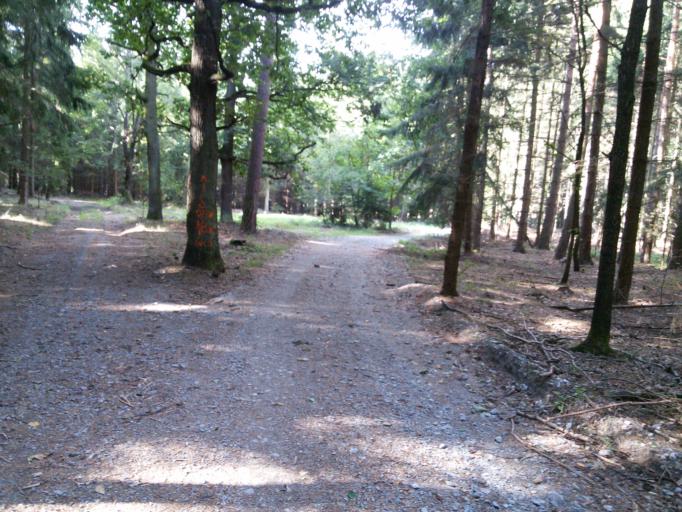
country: CZ
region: South Moravian
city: Cerna Hora
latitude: 49.3835
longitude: 16.5632
